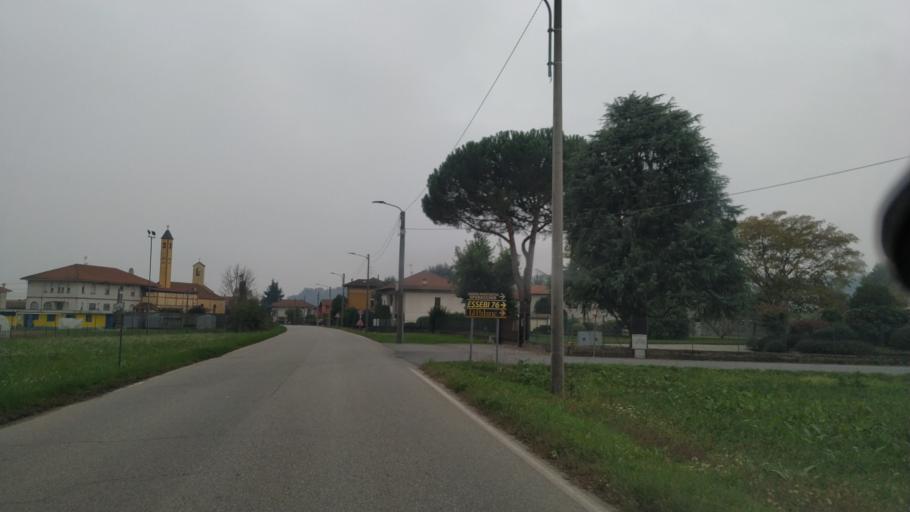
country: IT
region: Piedmont
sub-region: Provincia di Biella
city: Cerreto Castello
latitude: 45.5507
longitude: 8.1740
